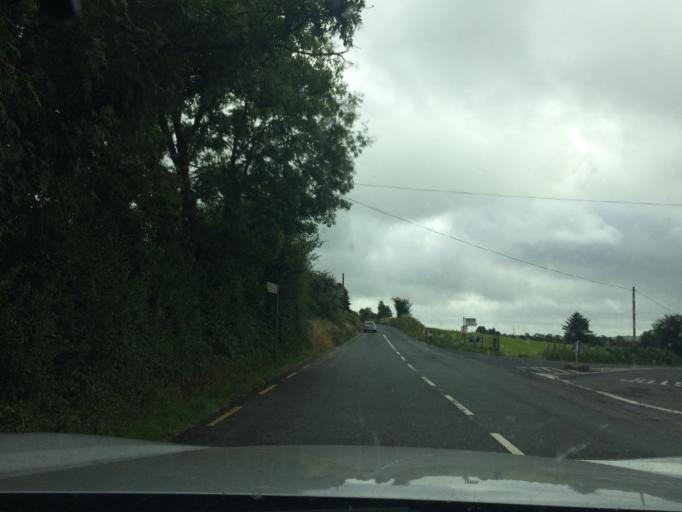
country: IE
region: Munster
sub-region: South Tipperary
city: Cluain Meala
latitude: 52.2301
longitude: -7.7194
